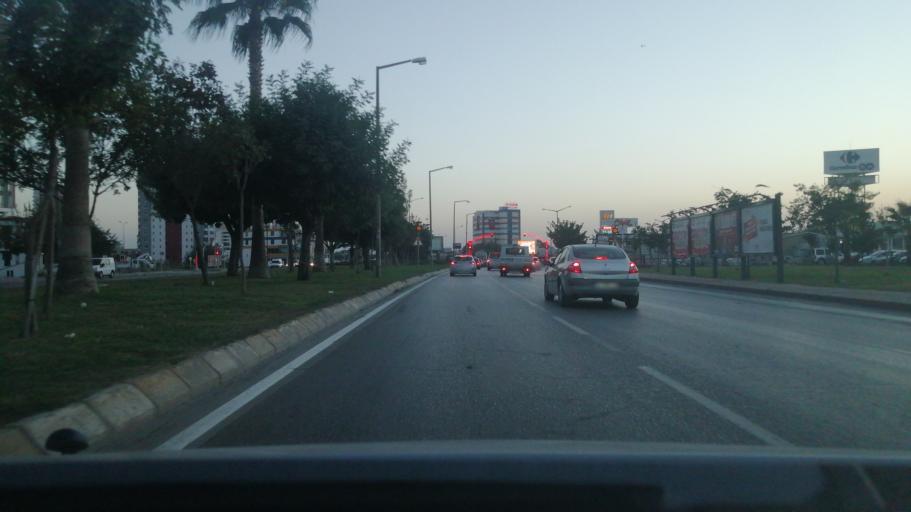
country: TR
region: Adana
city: Seyhan
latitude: 37.0172
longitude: 35.2515
